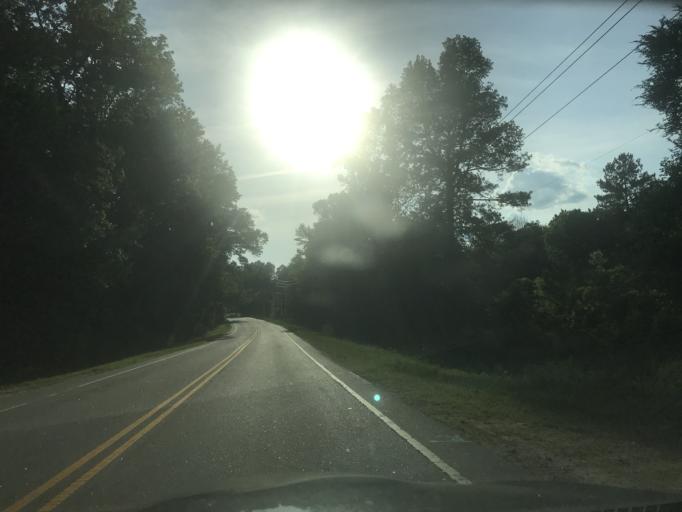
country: US
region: North Carolina
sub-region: Wake County
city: Knightdale
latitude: 35.7546
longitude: -78.5297
